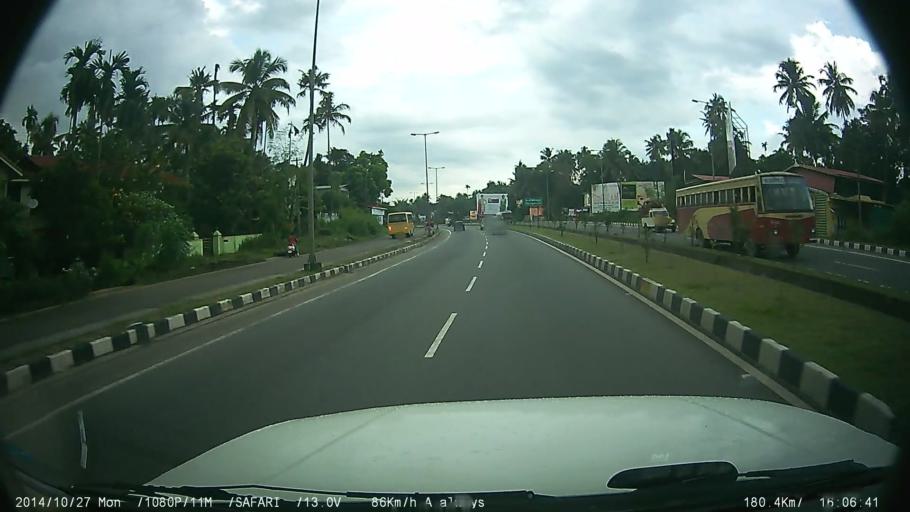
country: IN
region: Kerala
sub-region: Thrissur District
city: Kizhake Chalakudi
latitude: 10.3607
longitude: 76.3164
